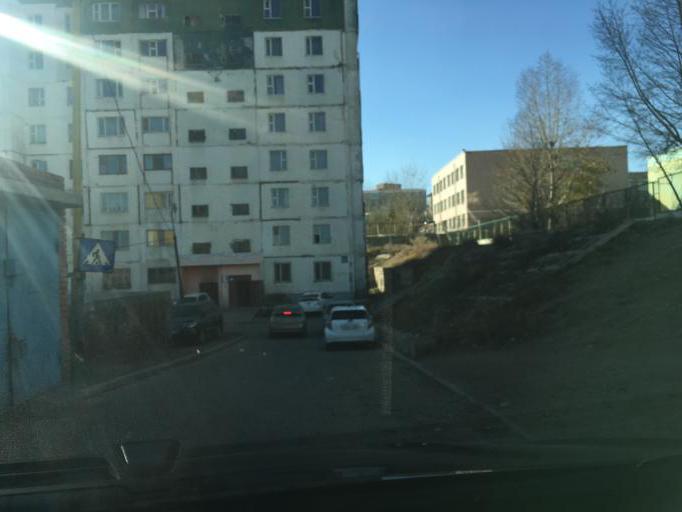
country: MN
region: Ulaanbaatar
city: Ulaanbaatar
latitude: 47.9255
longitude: 106.8680
